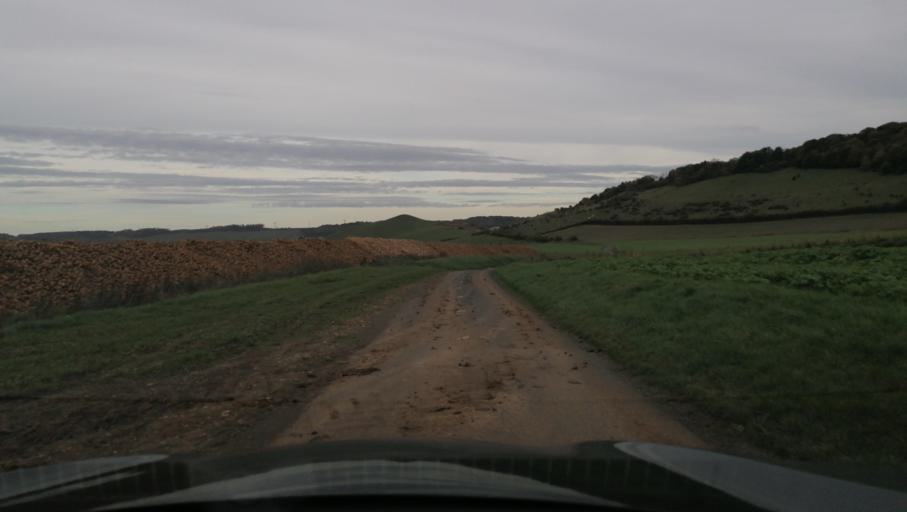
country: FR
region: Picardie
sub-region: Departement de la Somme
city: Bouttencourt
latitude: 49.8874
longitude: 1.6678
